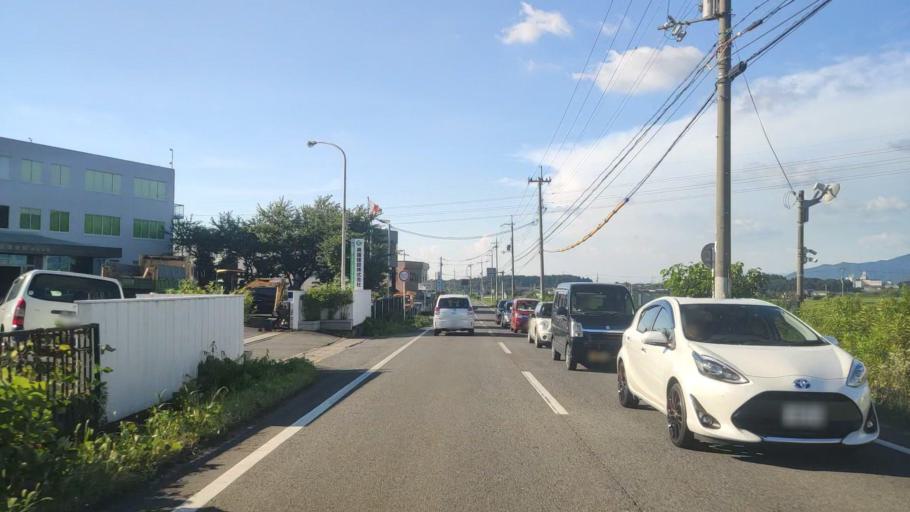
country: JP
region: Shiga Prefecture
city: Youkaichi
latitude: 35.0900
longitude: 136.2499
